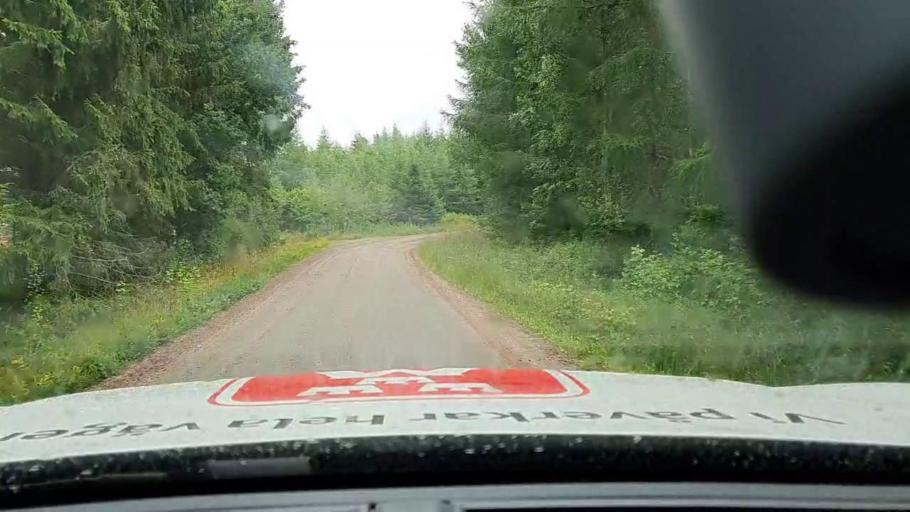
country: SE
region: Vaestra Goetaland
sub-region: Skara Kommun
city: Axvall
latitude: 58.4605
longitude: 13.6552
